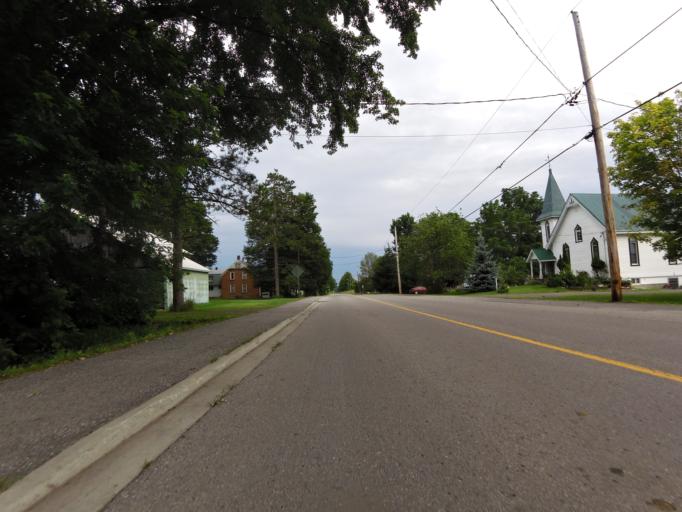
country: CA
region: Ontario
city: Perth
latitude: 45.0963
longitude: -76.3945
